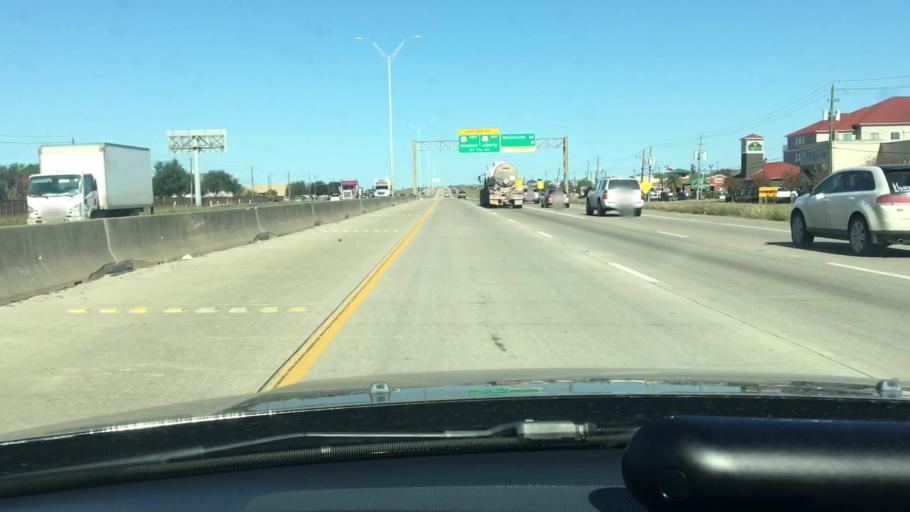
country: US
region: Texas
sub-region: Harris County
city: Cloverleaf
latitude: 29.8020
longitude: -95.1633
